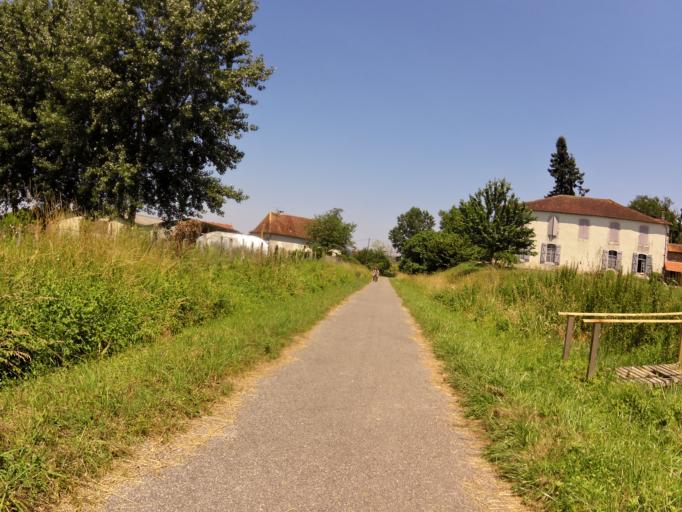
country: FR
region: Aquitaine
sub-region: Departement des Pyrenees-Atlantiques
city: Salies-de-Bearn
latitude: 43.4534
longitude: -0.9930
